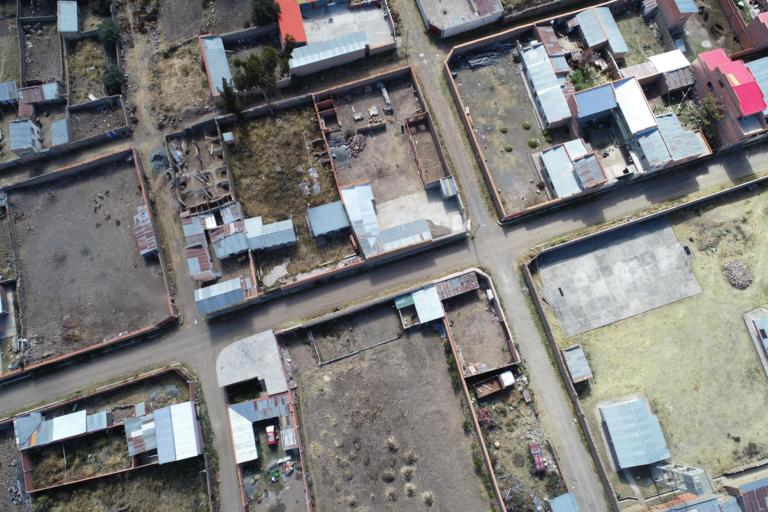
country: BO
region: La Paz
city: Achacachi
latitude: -15.8964
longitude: -68.9057
